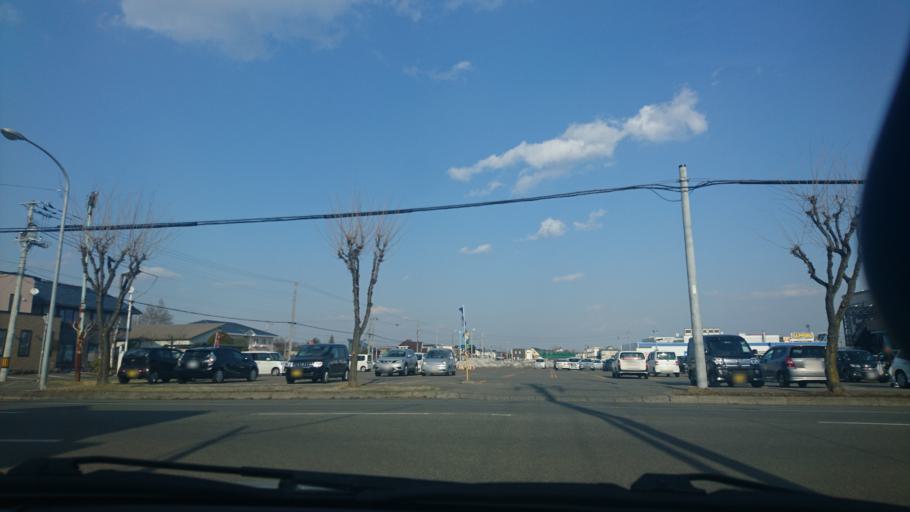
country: JP
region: Hokkaido
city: Obihiro
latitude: 42.9192
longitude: 143.1510
